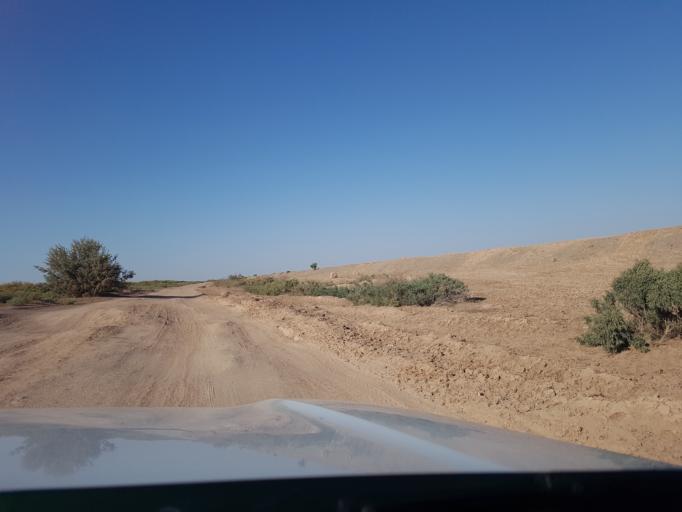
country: IR
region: Razavi Khorasan
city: Sarakhs
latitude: 36.9710
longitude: 61.3839
